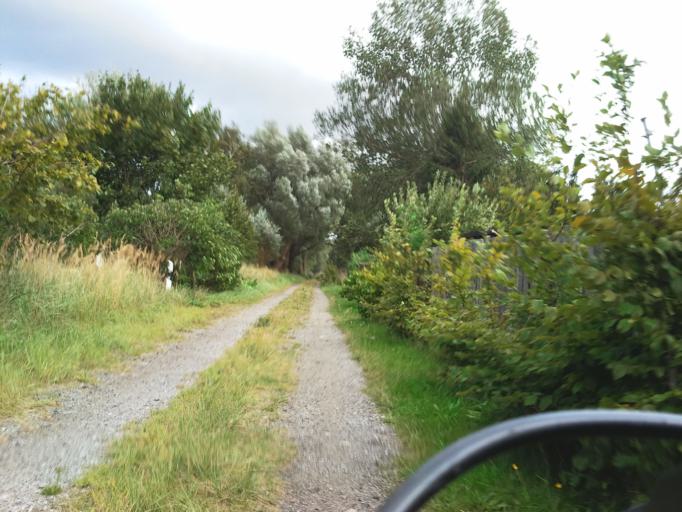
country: DE
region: Mecklenburg-Vorpommern
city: Rostock
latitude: 54.1118
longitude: 12.1090
